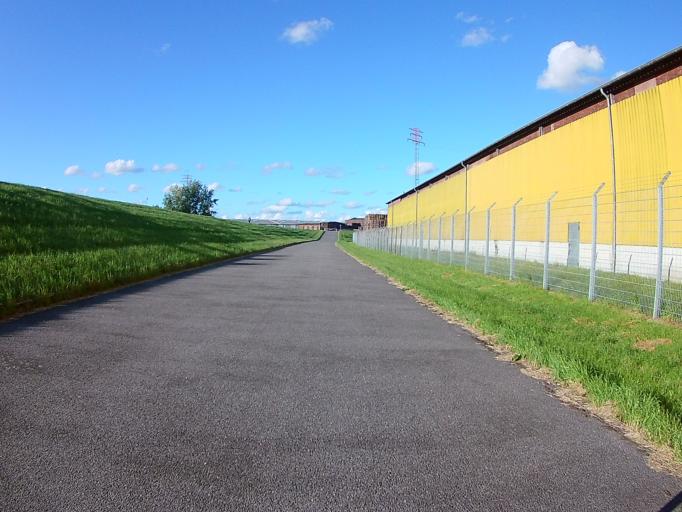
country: DE
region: Hamburg
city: Harburg
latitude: 53.4720
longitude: 9.9791
